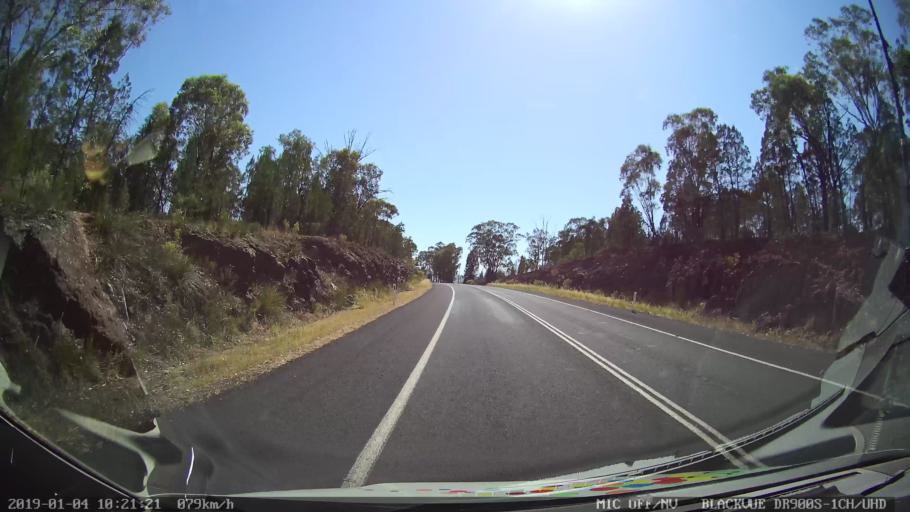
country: AU
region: New South Wales
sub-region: Cabonne
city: Canowindra
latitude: -33.3732
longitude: 148.5094
